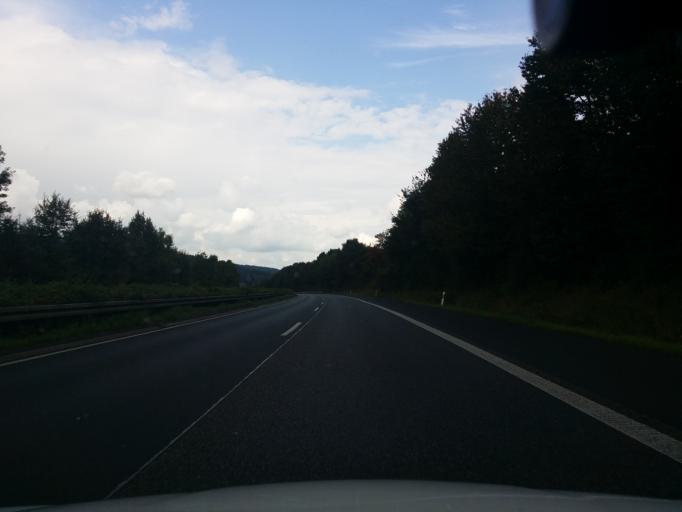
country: DE
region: Hesse
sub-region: Regierungsbezirk Darmstadt
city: Gelnhausen
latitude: 50.2126
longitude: 9.2376
